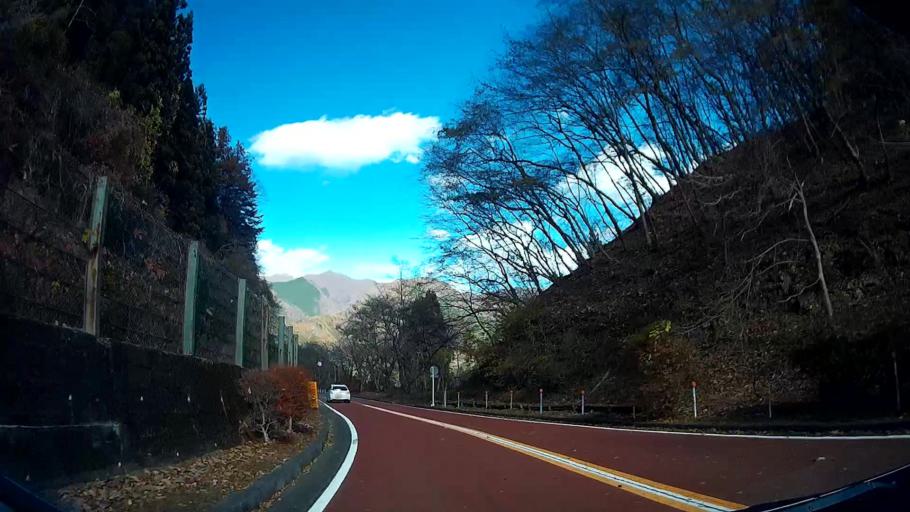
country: JP
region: Yamanashi
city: Uenohara
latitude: 35.7618
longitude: 139.0217
